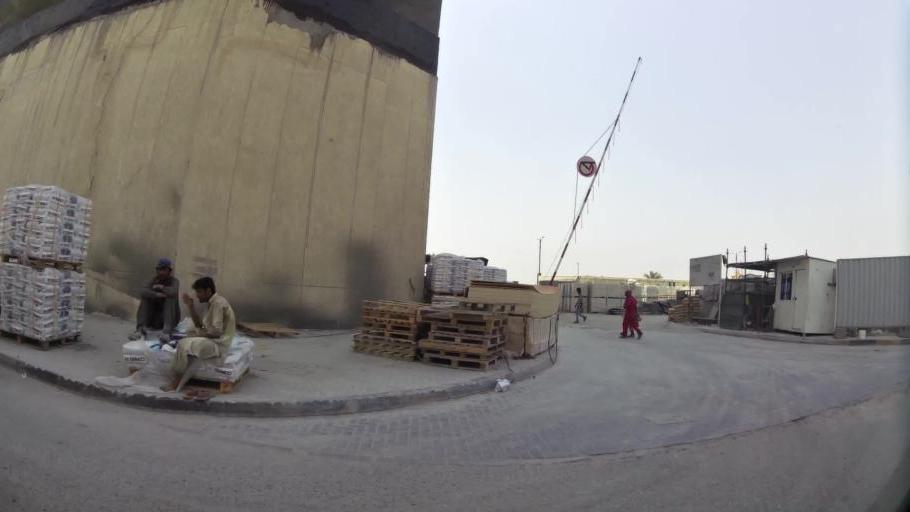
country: AE
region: Ajman
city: Ajman
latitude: 25.4056
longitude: 55.4315
